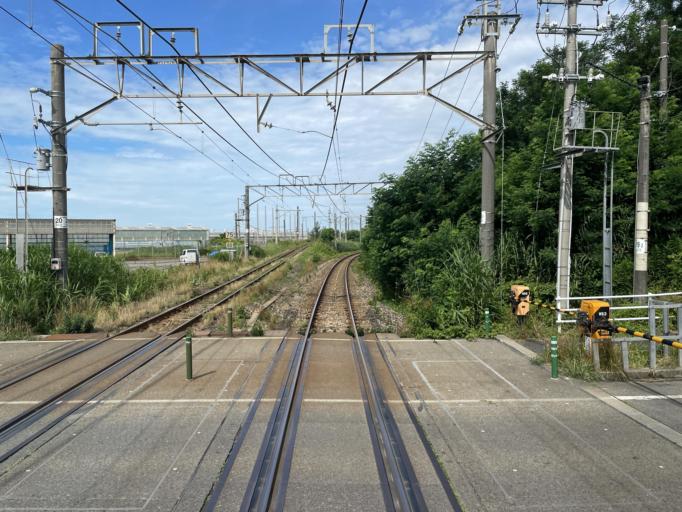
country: JP
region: Niigata
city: Kameda-honcho
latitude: 37.9036
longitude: 139.0933
